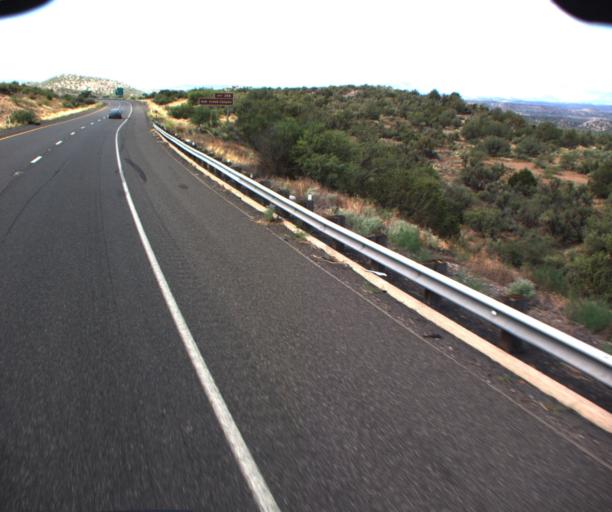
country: US
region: Arizona
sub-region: Yavapai County
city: Lake Montezuma
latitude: 34.7014
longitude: -111.7432
